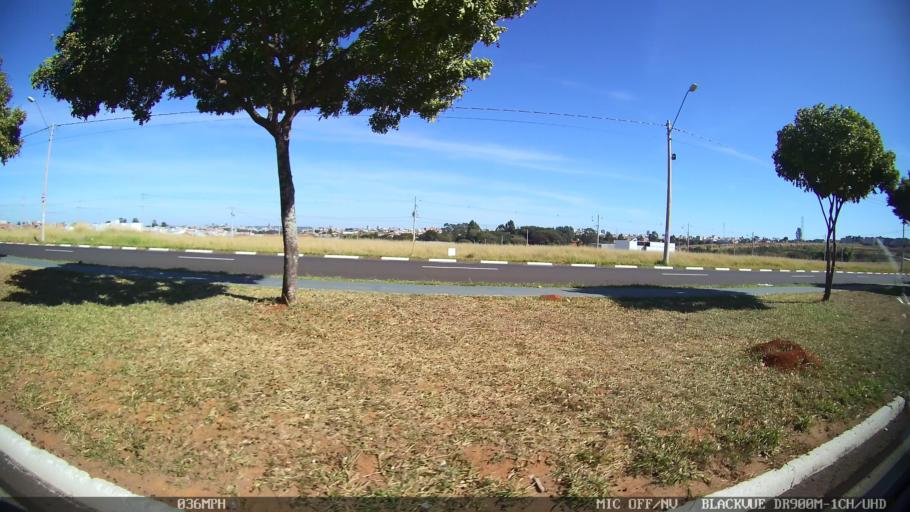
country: BR
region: Sao Paulo
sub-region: Franca
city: Franca
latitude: -20.5464
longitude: -47.3598
